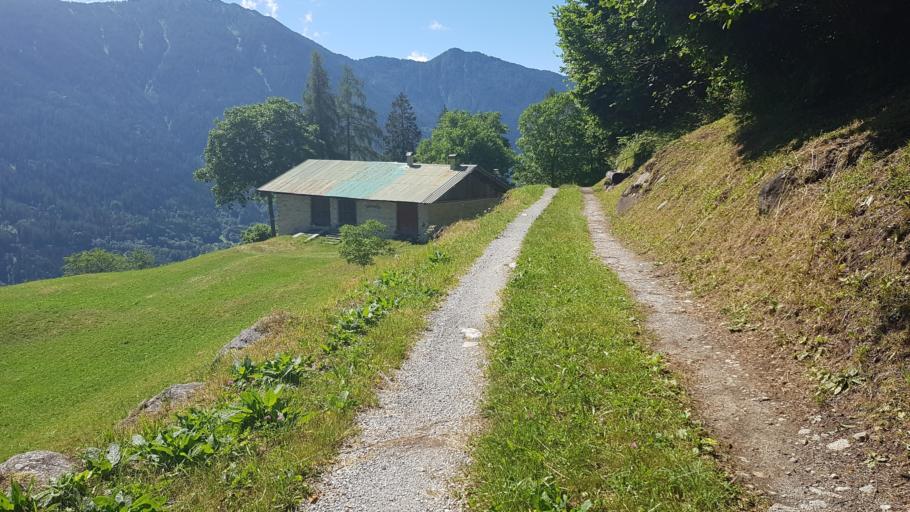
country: IT
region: Trentino-Alto Adige
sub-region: Provincia di Trento
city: Caderzone Terme
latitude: 46.1469
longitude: 10.7493
